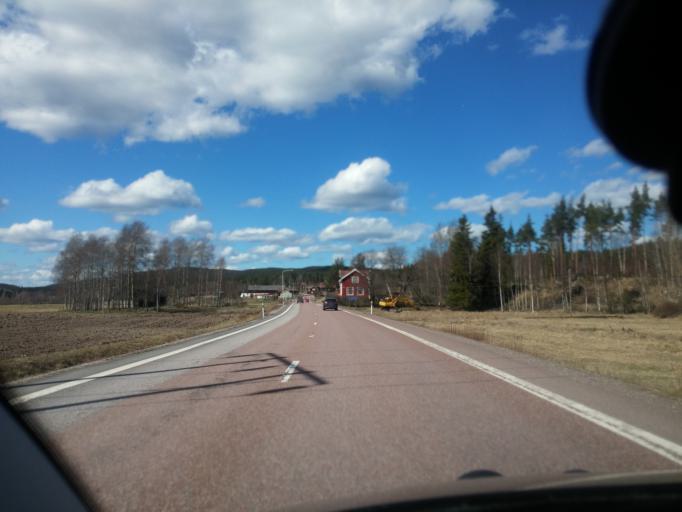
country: SE
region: Dalarna
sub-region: Faluns Kommun
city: Svardsjo
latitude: 60.7196
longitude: 15.7773
